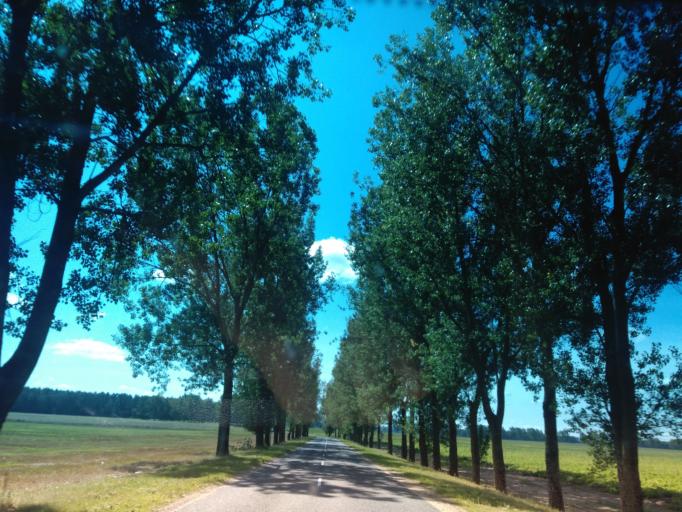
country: BY
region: Minsk
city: Uzda
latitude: 53.2802
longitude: 27.2299
